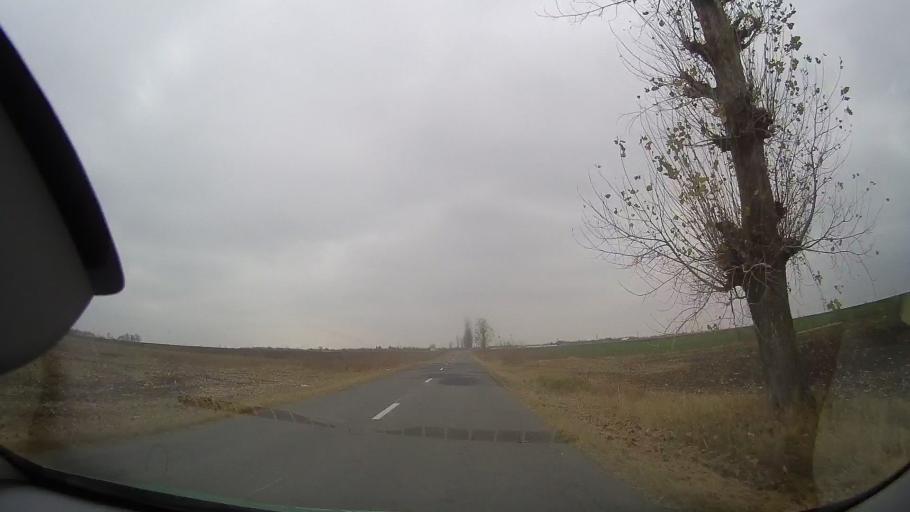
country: RO
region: Ialomita
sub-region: Comuna Valea Macrisului
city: Valea Macrisului
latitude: 44.7354
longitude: 26.8517
